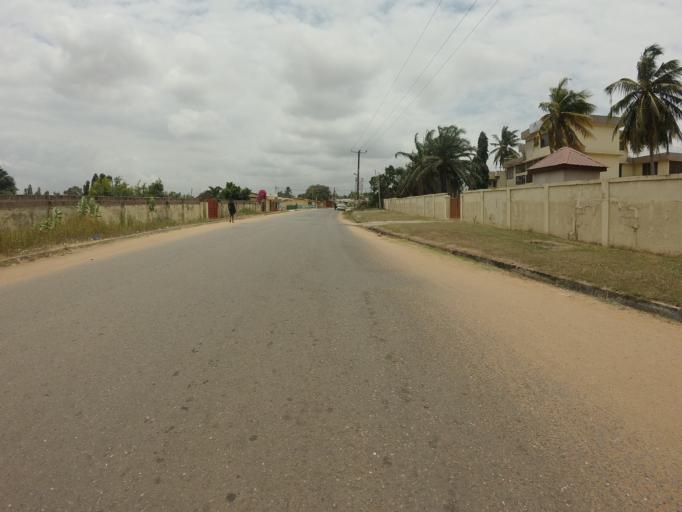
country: GH
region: Greater Accra
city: Nungua
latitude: 5.6140
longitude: -0.0783
